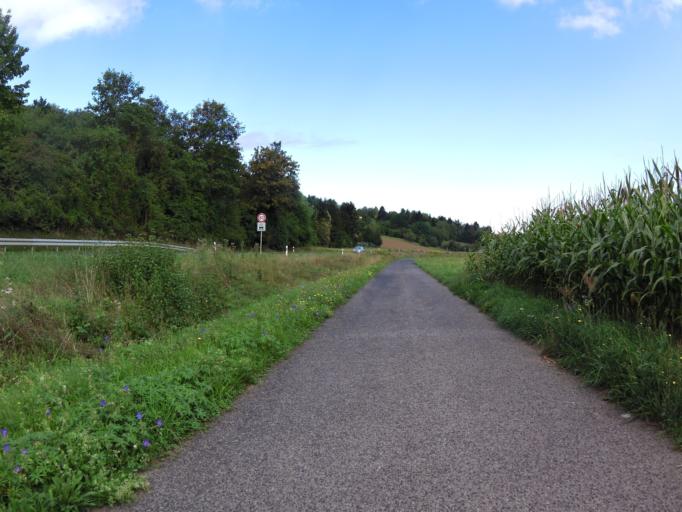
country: DE
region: Bavaria
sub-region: Regierungsbezirk Unterfranken
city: Kitzingen
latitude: 49.7560
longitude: 10.1537
